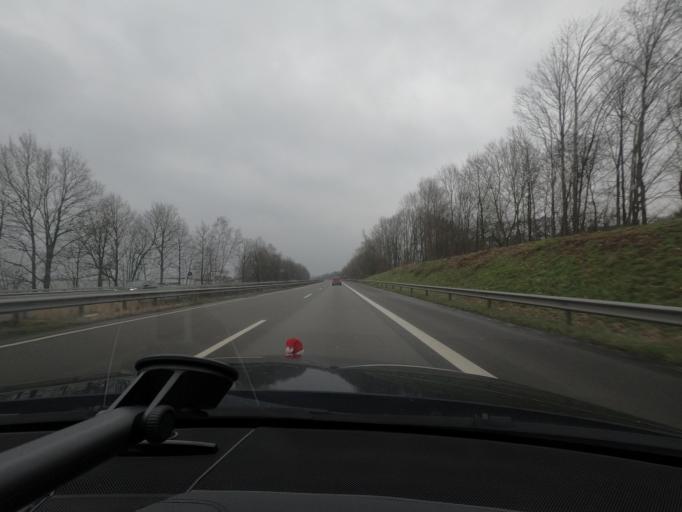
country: DE
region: Lower Saxony
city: Seevetal
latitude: 53.3881
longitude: 10.0017
